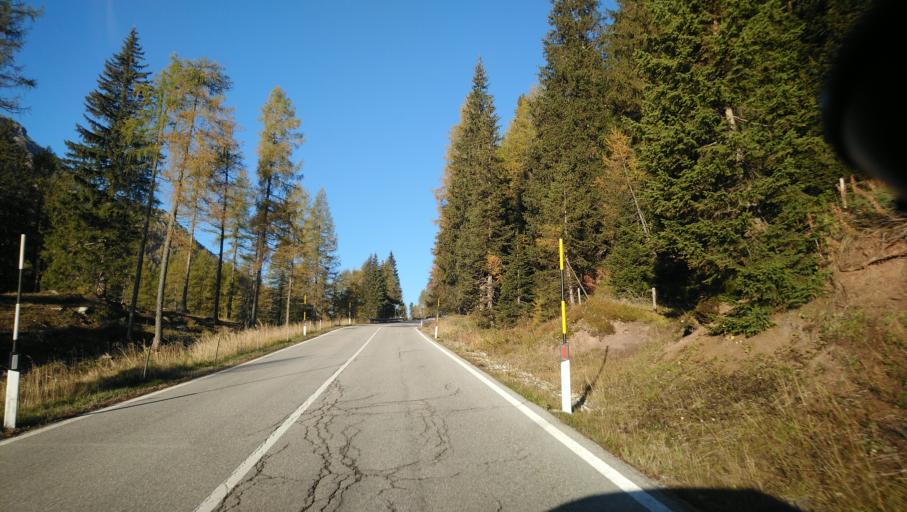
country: IT
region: Veneto
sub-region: Provincia di Belluno
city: Falcade Alto
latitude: 46.3789
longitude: 11.8133
